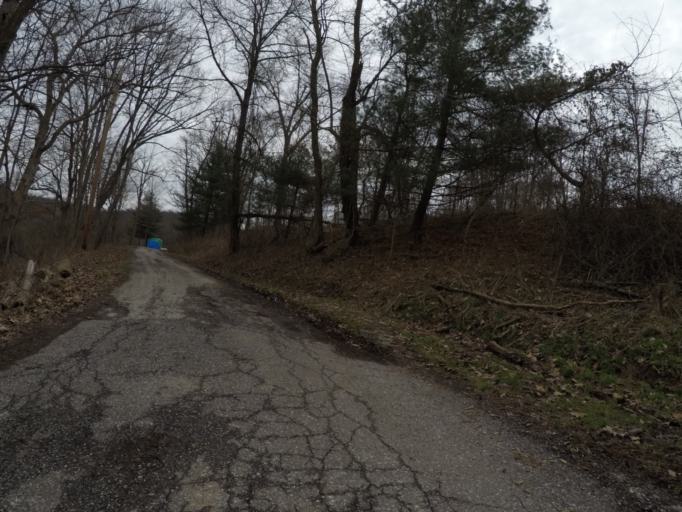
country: US
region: Ohio
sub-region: Lawrence County
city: Burlington
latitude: 38.3919
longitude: -82.5192
